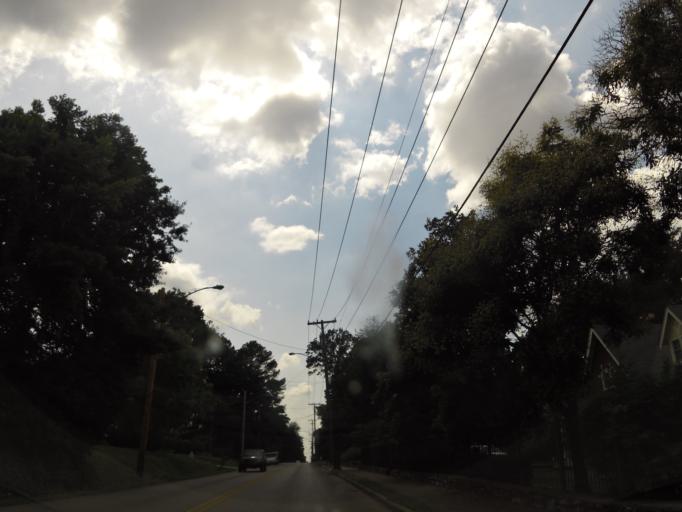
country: US
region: Tennessee
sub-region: Davidson County
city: Oak Hill
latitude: 36.1208
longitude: -86.7798
